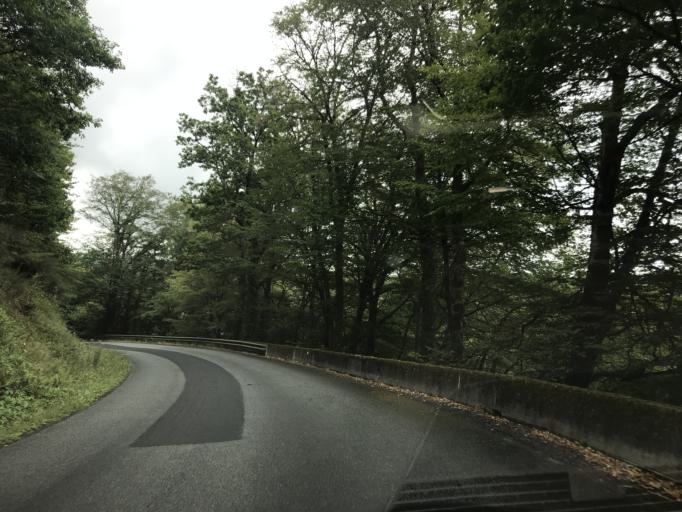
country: FR
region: Auvergne
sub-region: Departement du Cantal
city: Pleaux
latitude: 45.2369
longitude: 2.1759
